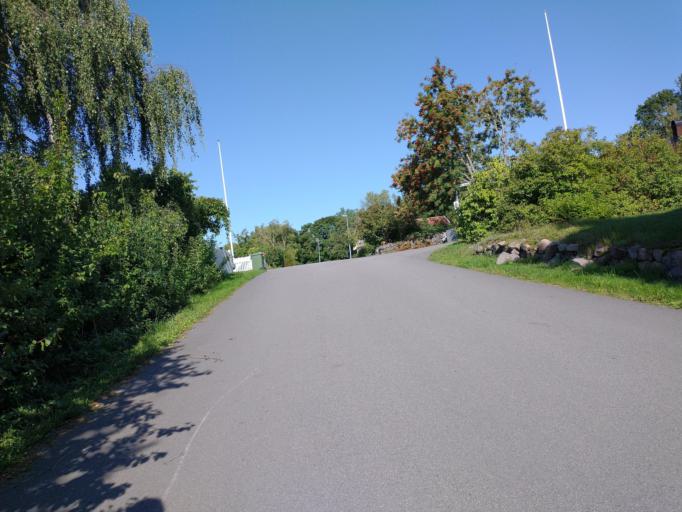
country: SE
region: Kalmar
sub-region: Kalmar Kommun
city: Lindsdal
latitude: 56.7820
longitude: 16.2820
